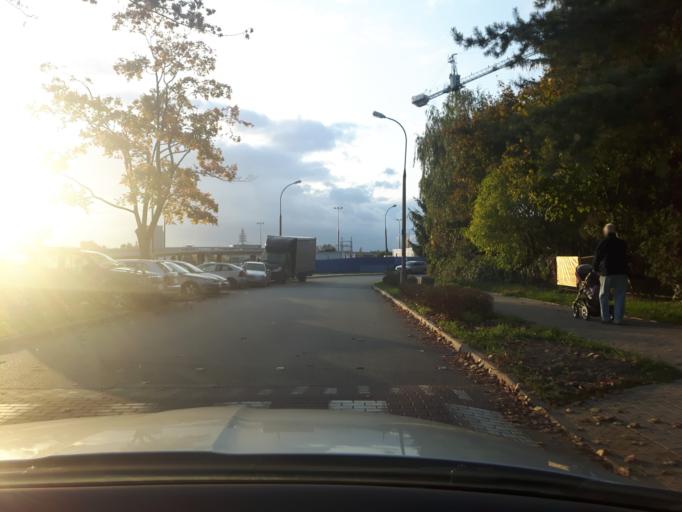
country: PL
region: Masovian Voivodeship
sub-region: Warszawa
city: Ursynow
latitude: 52.1526
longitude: 21.0209
